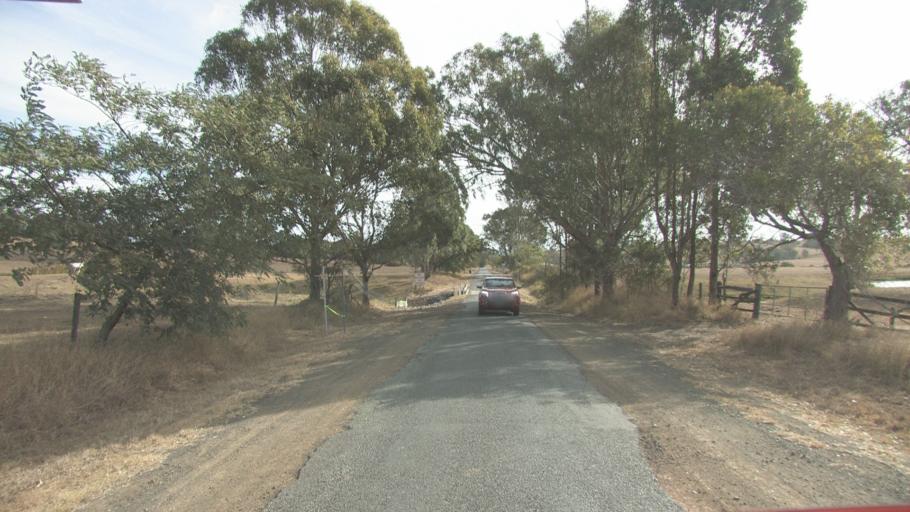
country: AU
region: Queensland
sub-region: Logan
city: Cedar Vale
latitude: -27.9201
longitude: 153.0093
